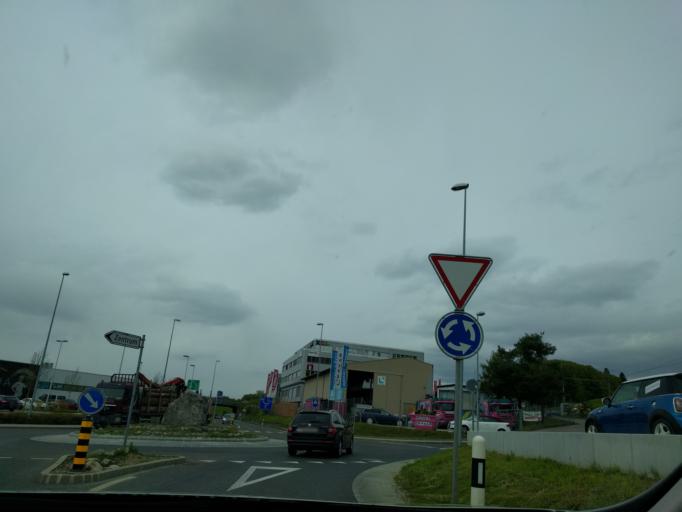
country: CH
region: Fribourg
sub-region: Sense District
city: Dudingen
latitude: 46.8584
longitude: 7.2007
